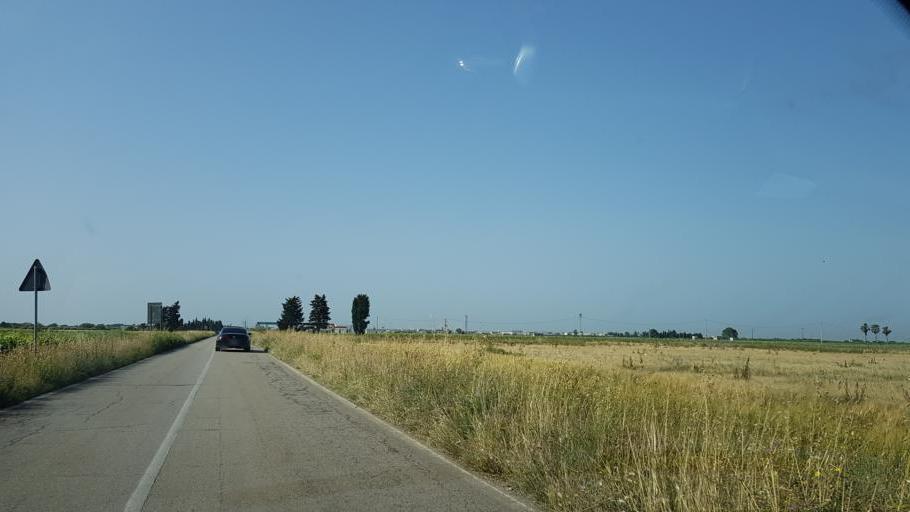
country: IT
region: Apulia
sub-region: Provincia di Brindisi
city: San Pancrazio Salentino
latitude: 40.4347
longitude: 17.8396
